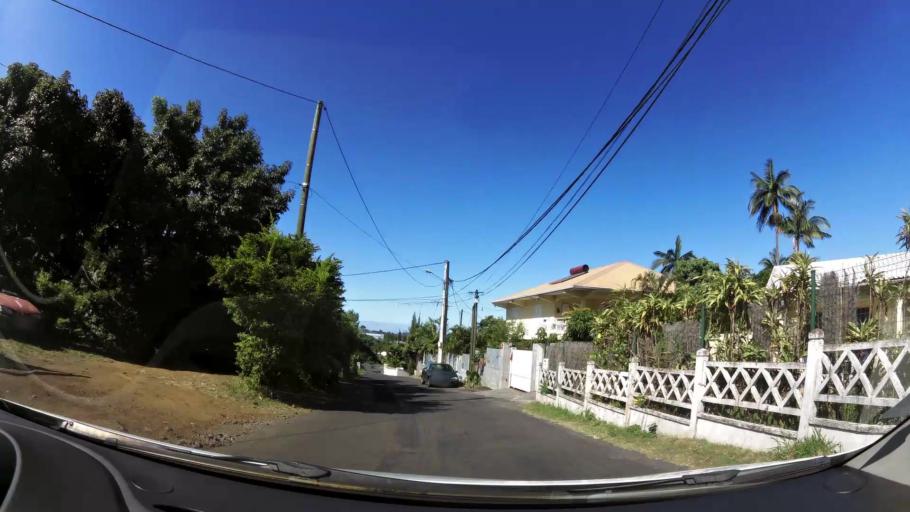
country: RE
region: Reunion
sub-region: Reunion
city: Le Tampon
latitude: -21.2638
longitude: 55.5032
